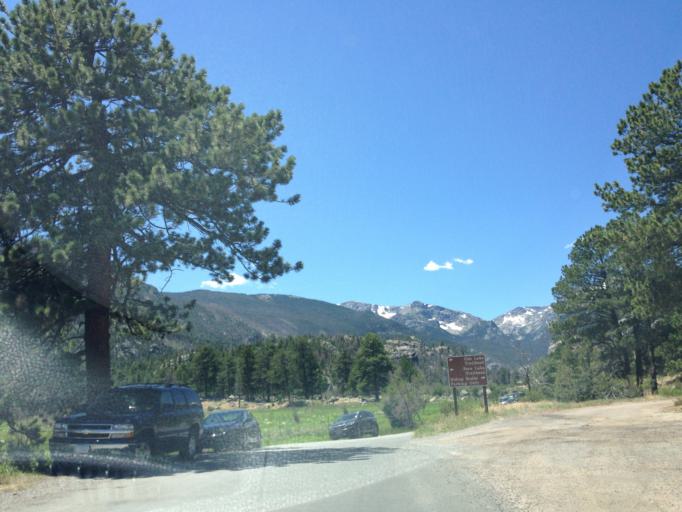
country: US
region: Colorado
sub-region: Larimer County
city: Estes Park
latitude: 40.3569
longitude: -105.6121
